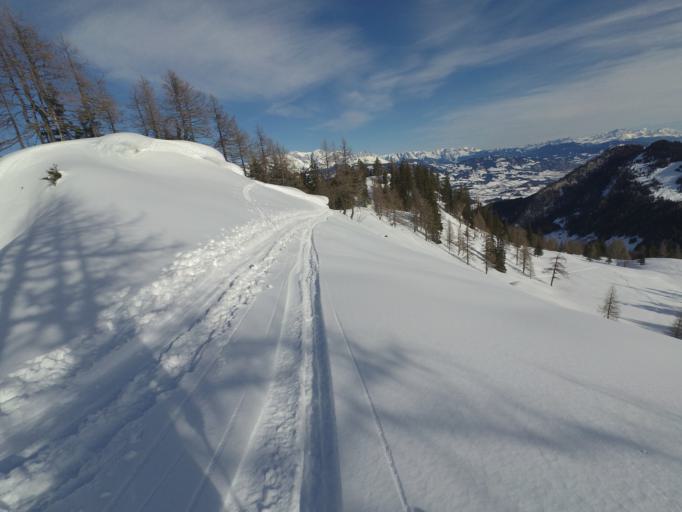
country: AT
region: Salzburg
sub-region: Politischer Bezirk Zell am See
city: Rauris
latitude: 47.2643
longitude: 13.0185
